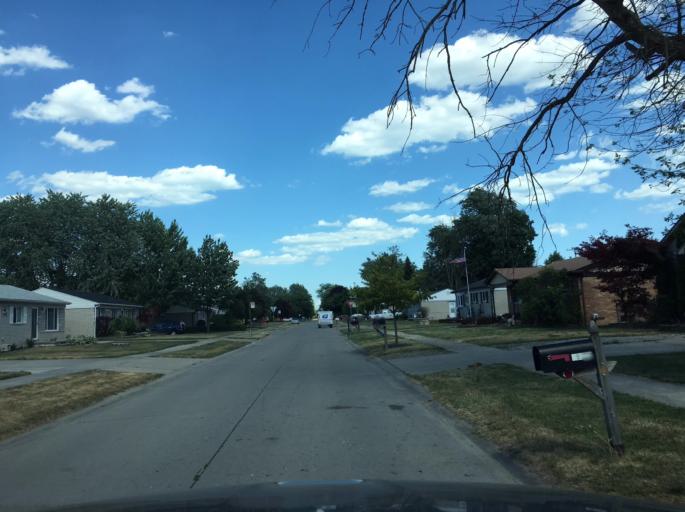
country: US
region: Michigan
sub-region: Macomb County
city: Fraser
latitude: 42.5418
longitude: -82.9174
